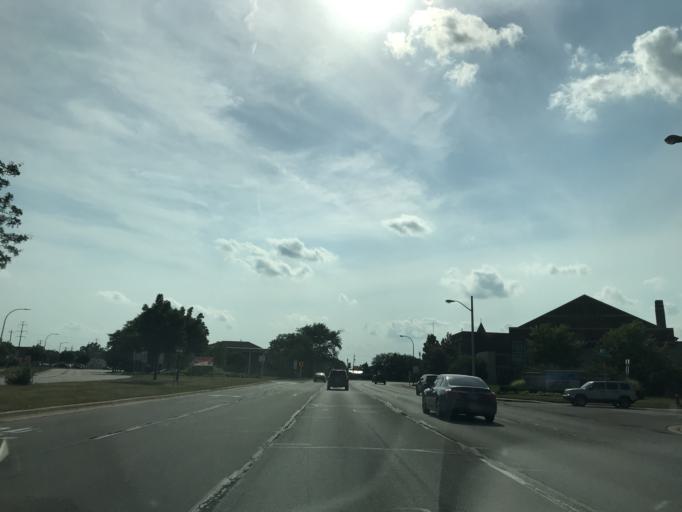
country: US
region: Michigan
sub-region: Wayne County
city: Wayne
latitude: 42.2815
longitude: -83.3770
